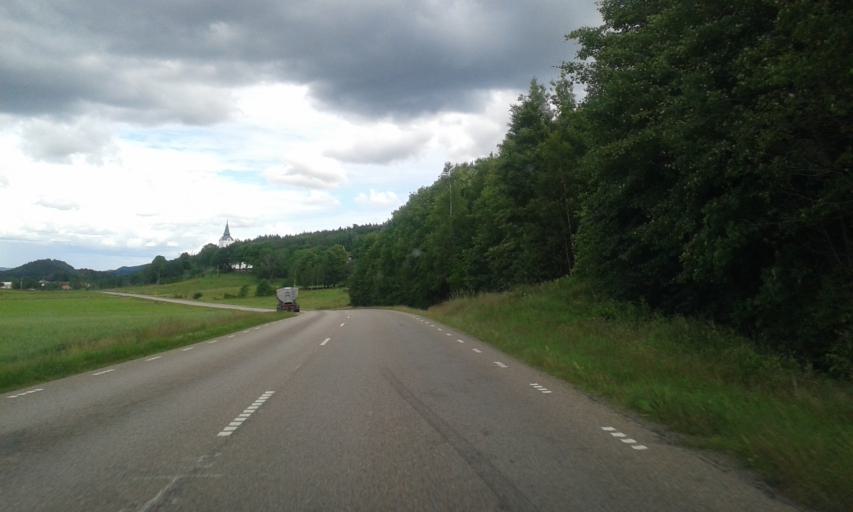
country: SE
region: Vaestra Goetaland
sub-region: Lilla Edets Kommun
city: Lilla Edet
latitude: 58.0856
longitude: 12.1171
